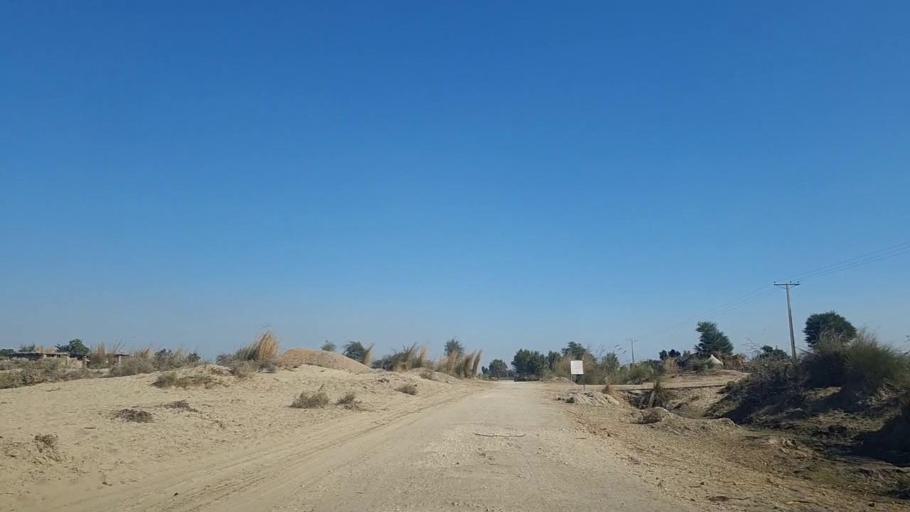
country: PK
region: Sindh
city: Khadro
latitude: 26.2093
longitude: 68.8771
